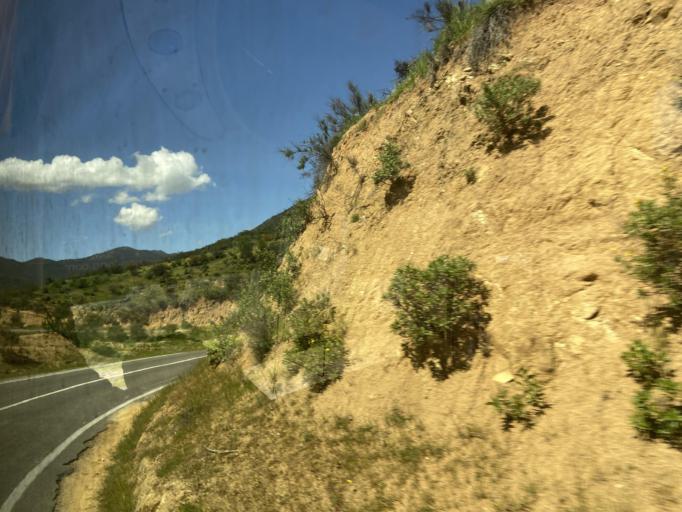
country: CL
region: Valparaiso
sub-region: Provincia de Marga Marga
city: Villa Alemana
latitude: -33.1892
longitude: -71.2914
